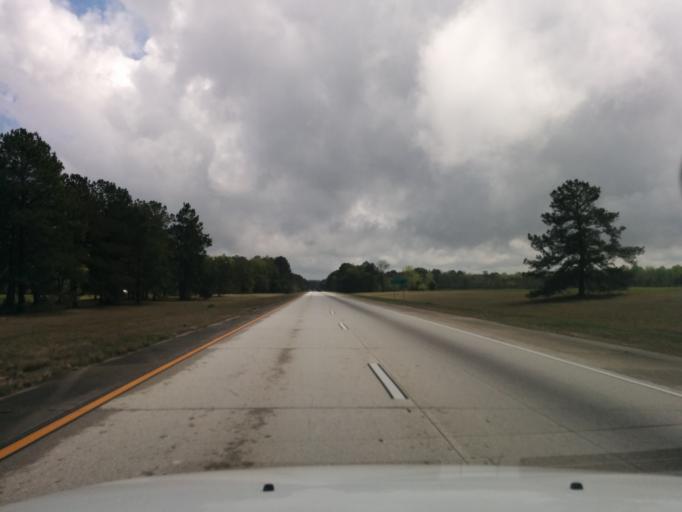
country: US
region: Georgia
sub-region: Candler County
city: Metter
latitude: 32.3325
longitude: -81.9420
